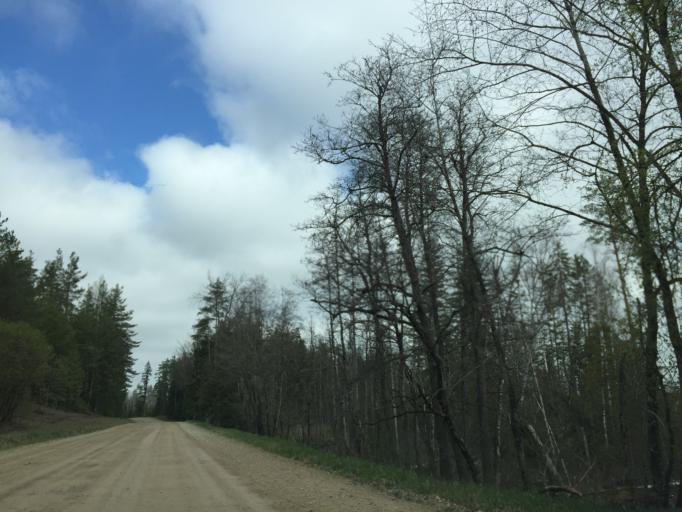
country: EE
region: Valgamaa
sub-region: Valga linn
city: Valga
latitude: 57.6205
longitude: 26.2363
